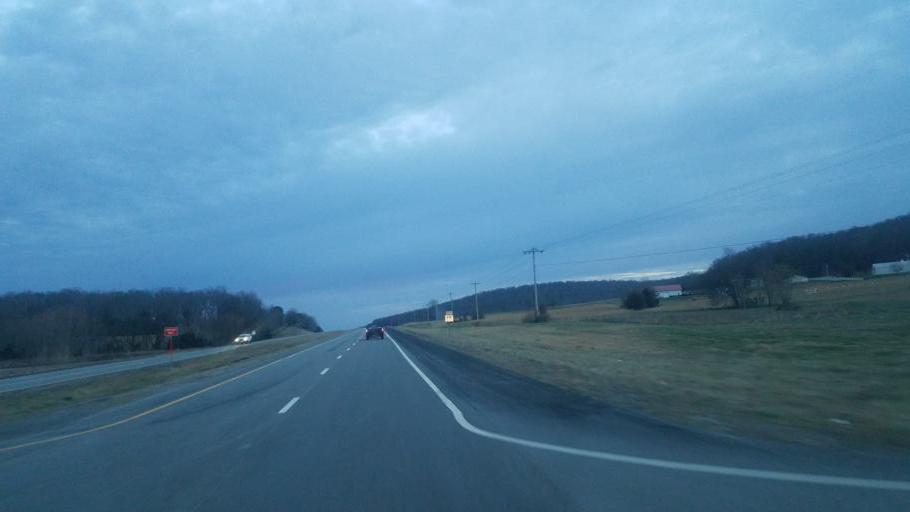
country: US
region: Tennessee
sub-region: Van Buren County
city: Spencer
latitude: 35.8348
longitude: -85.4634
